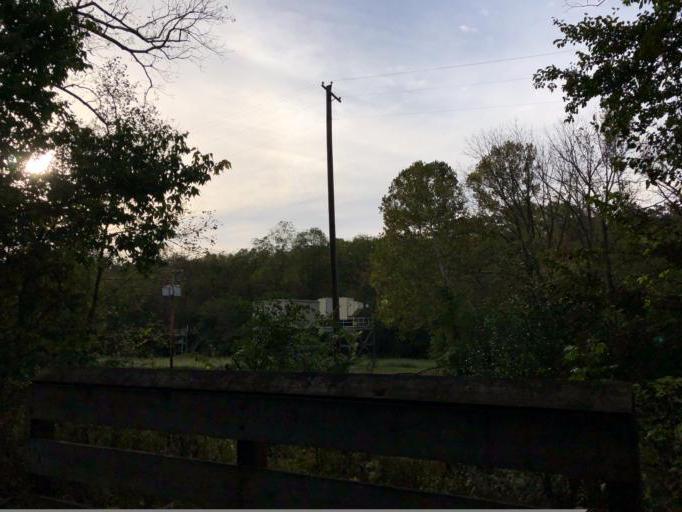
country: US
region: Ohio
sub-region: Warren County
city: Kings Mills
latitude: 39.3482
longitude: -84.2517
